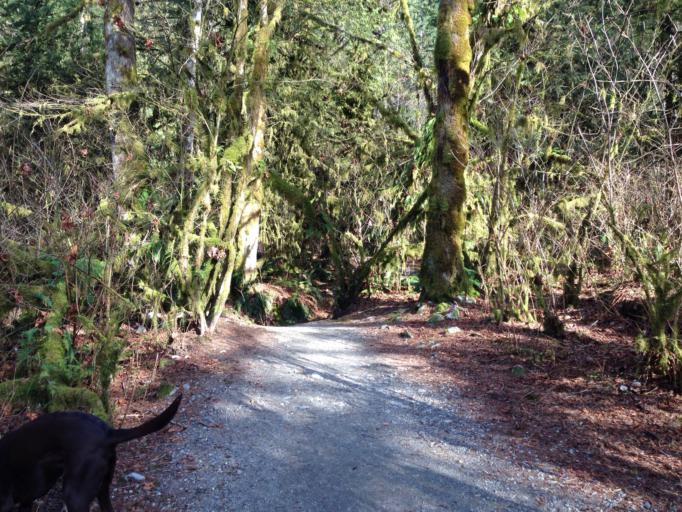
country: CA
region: British Columbia
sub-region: Greater Vancouver Regional District
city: Anmore
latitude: 49.3388
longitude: -122.8561
